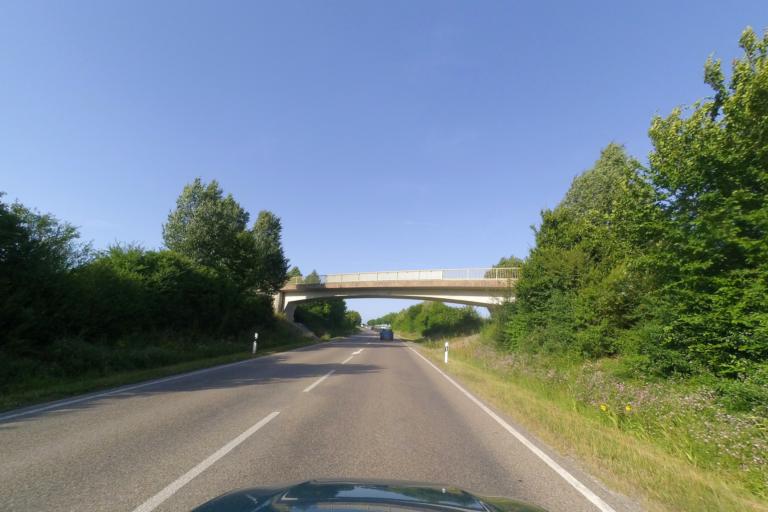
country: DE
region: Bavaria
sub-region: Swabia
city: Lauingen
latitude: 48.5687
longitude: 10.3994
